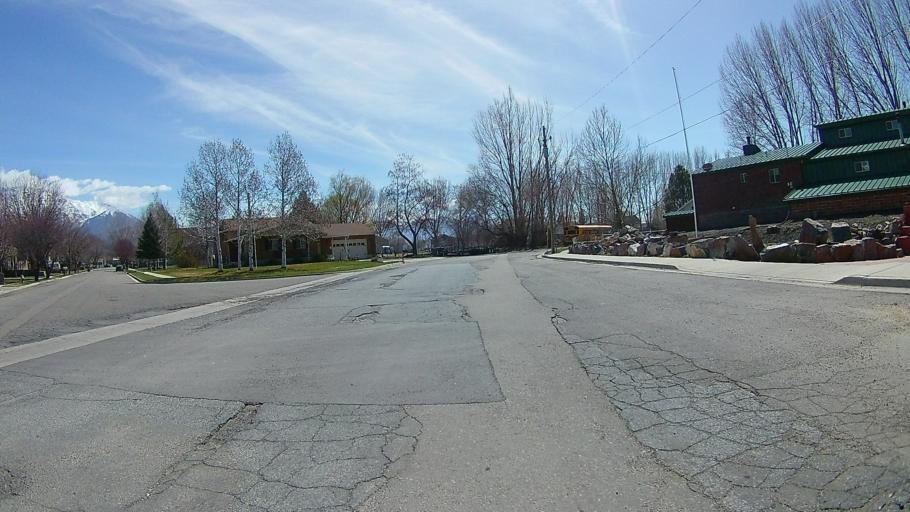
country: US
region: Utah
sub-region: Utah County
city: American Fork
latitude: 40.3663
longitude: -111.8055
